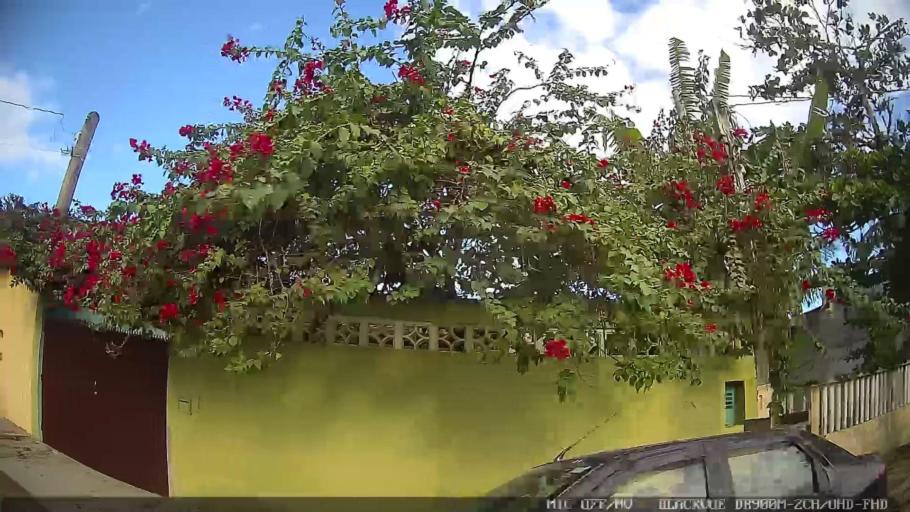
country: BR
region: Sao Paulo
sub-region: Itanhaem
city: Itanhaem
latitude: -24.2117
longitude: -46.8411
